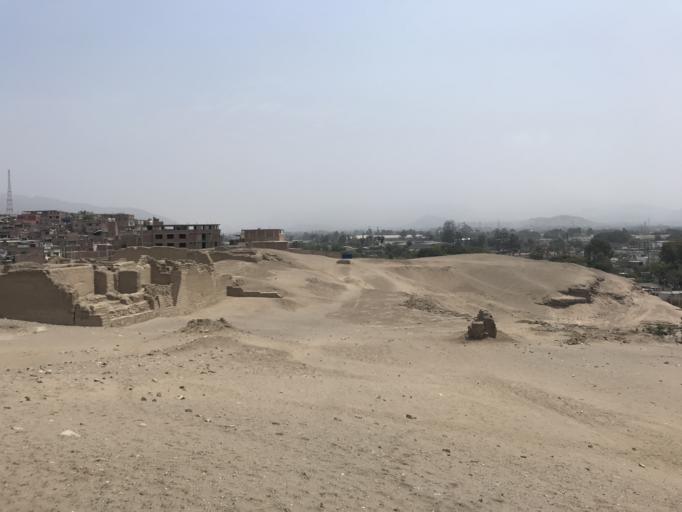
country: PE
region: Lima
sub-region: Lima
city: Punta Hermosa
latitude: -12.2553
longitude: -76.8962
